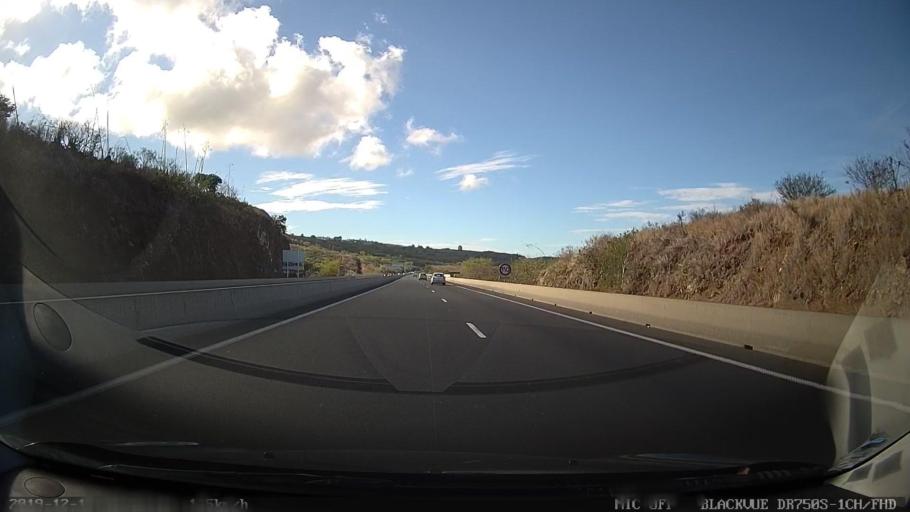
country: RE
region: Reunion
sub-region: Reunion
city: Saint-Paul
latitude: -21.0519
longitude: 55.2478
